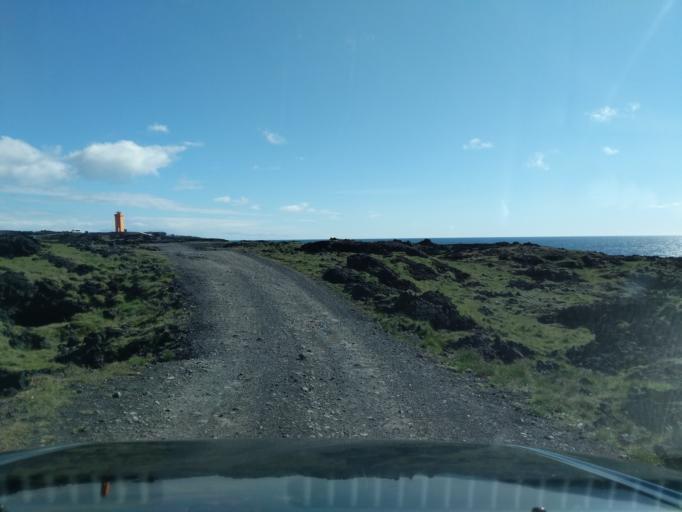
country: IS
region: West
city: Olafsvik
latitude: 64.8671
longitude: -24.0395
